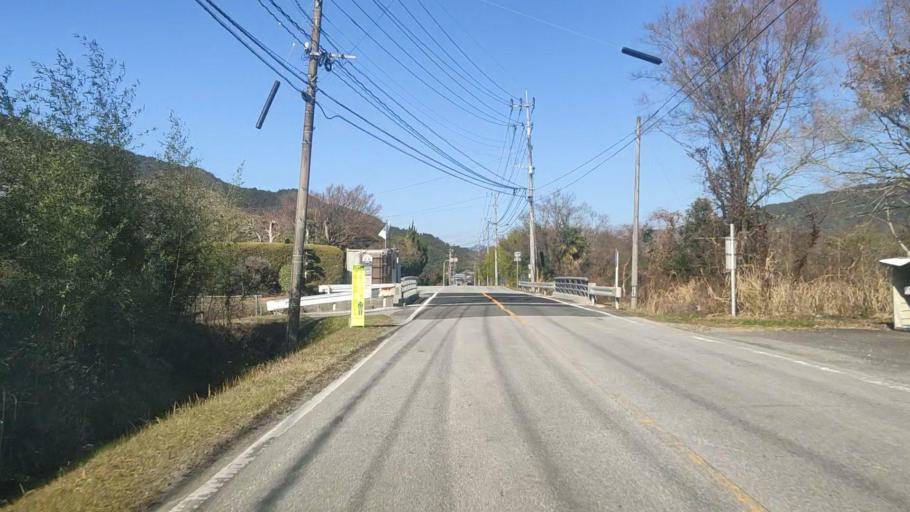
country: JP
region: Oita
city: Saiki
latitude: 32.9105
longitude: 131.9300
